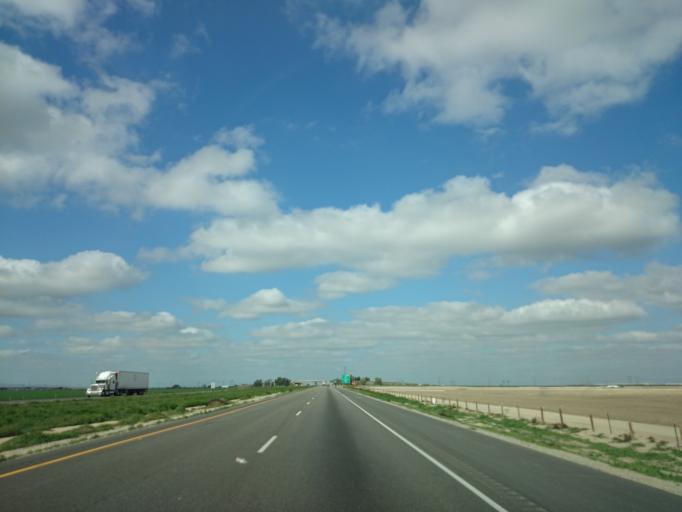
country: US
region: California
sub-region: Kern County
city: Greenfield
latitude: 35.2033
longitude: -119.1565
